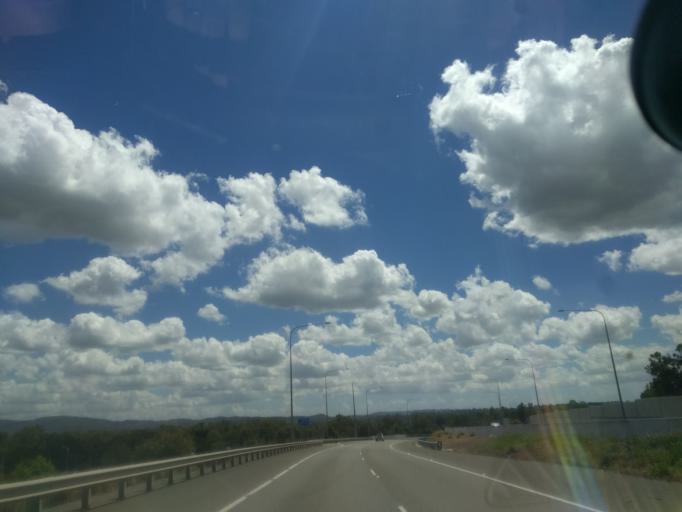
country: AU
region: Queensland
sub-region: Ipswich
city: Riverview
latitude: -27.5983
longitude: 152.8343
